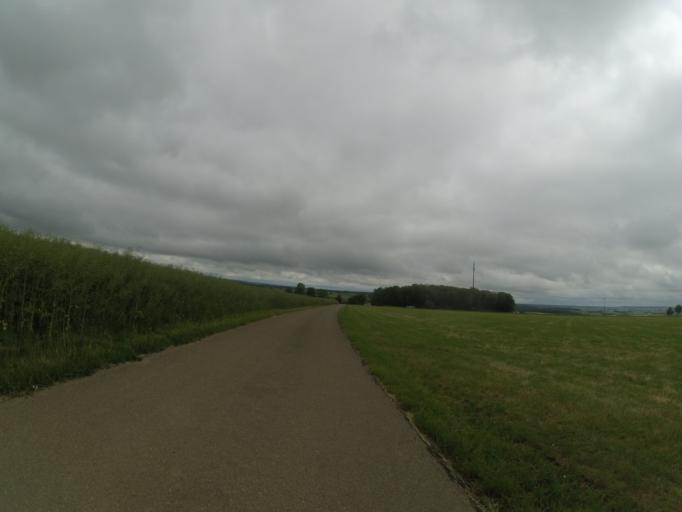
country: DE
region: Baden-Wuerttemberg
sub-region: Tuebingen Region
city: Bernstadt
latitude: 48.4770
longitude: 10.0535
